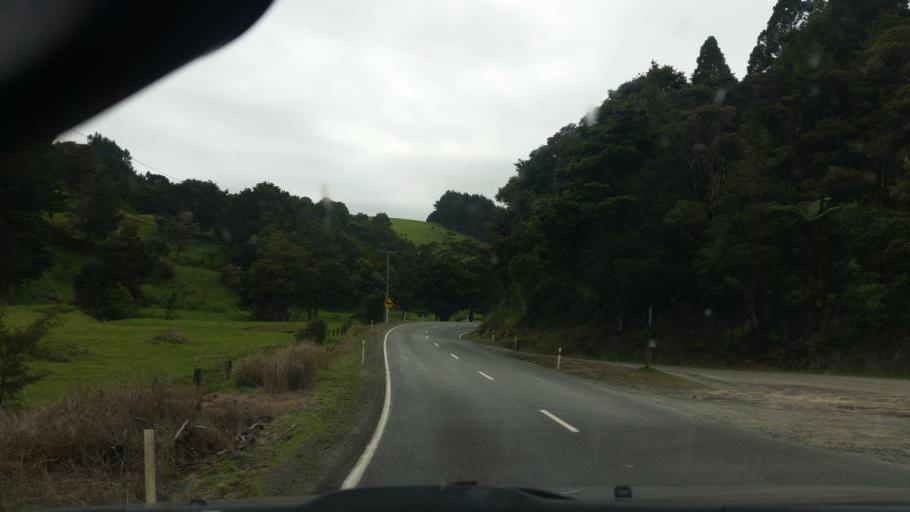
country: NZ
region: Northland
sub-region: Kaipara District
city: Dargaville
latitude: -35.8120
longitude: 173.7275
